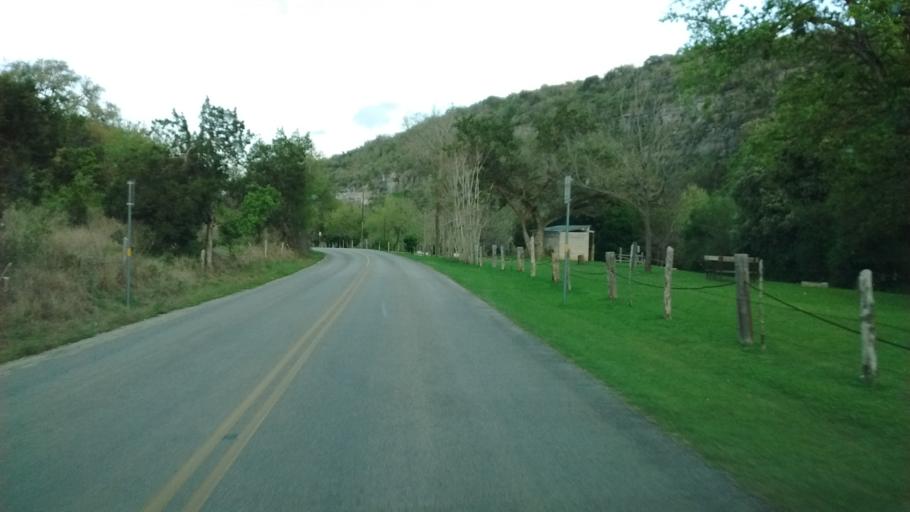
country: US
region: Texas
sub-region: Comal County
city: New Braunfels
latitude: 29.7646
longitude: -98.1561
